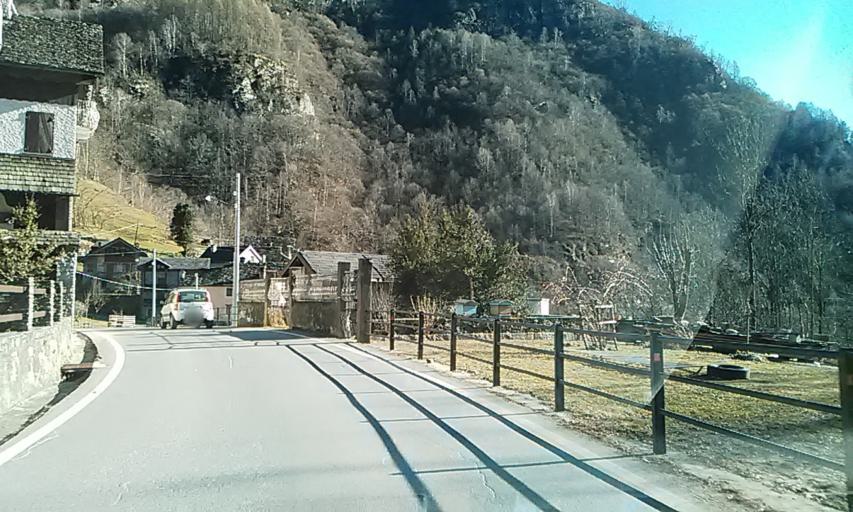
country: IT
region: Piedmont
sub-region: Provincia di Vercelli
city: Boccioleto
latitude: 45.8384
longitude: 8.0846
